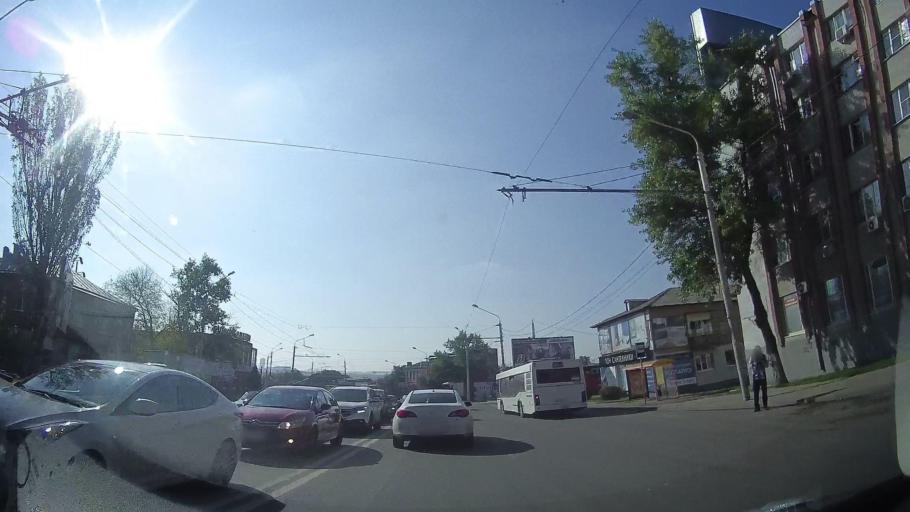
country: RU
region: Rostov
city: Severnyy
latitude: 47.2656
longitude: 39.6827
